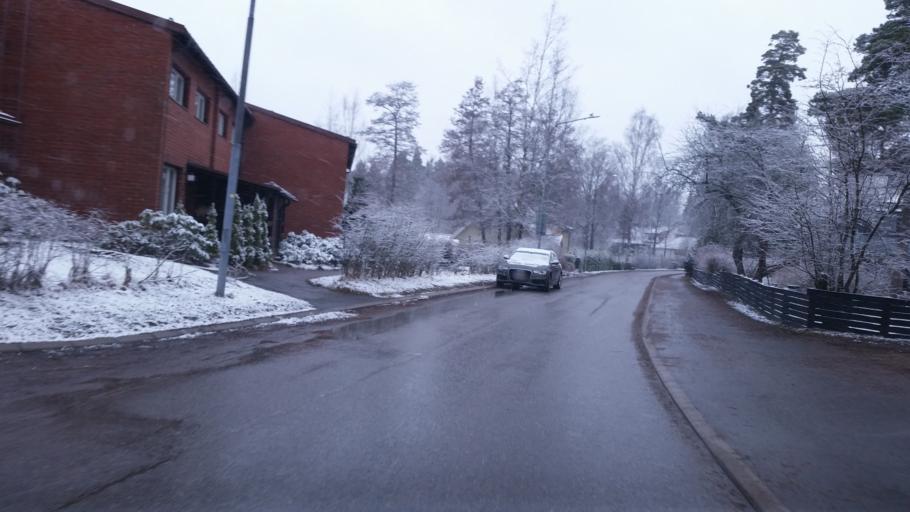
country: FI
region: Uusimaa
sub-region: Helsinki
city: Koukkuniemi
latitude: 60.1624
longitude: 24.7602
